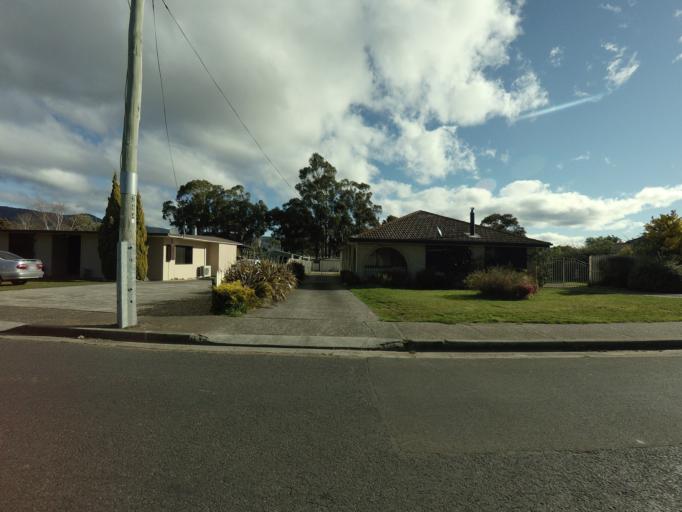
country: AU
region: Tasmania
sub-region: Derwent Valley
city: New Norfolk
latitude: -42.7684
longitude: 147.0459
